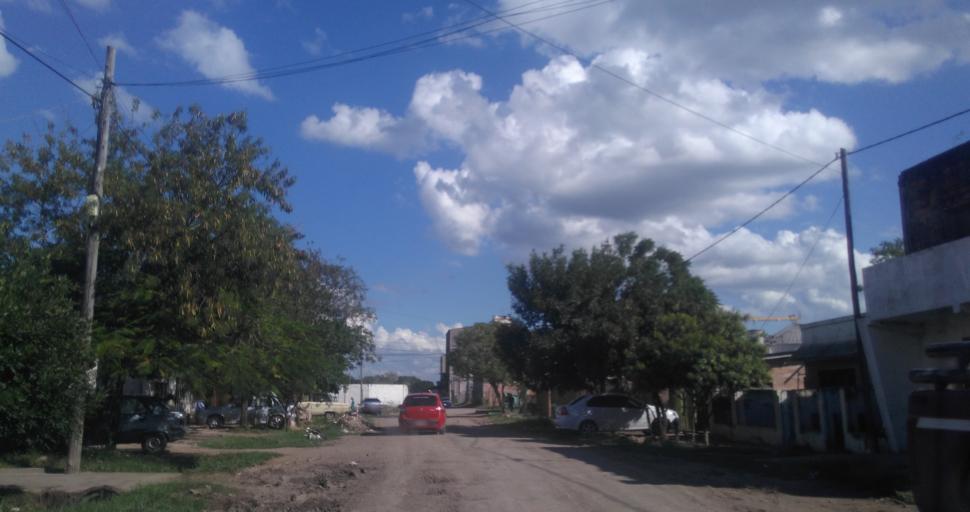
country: AR
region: Chaco
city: Resistencia
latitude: -27.4749
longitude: -58.9649
